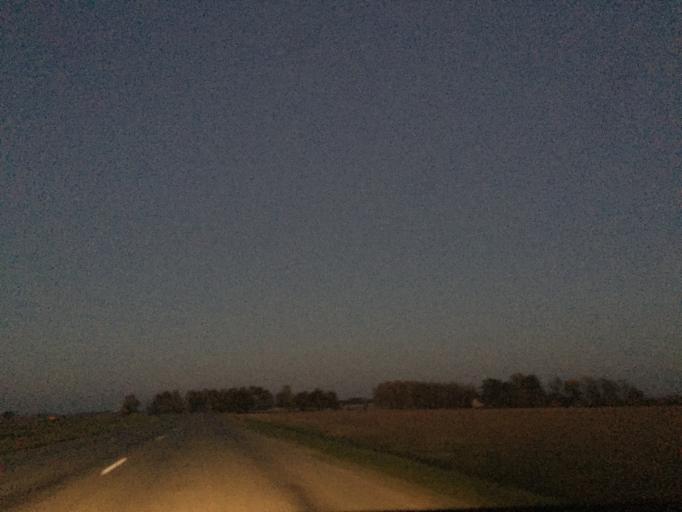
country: LV
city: Tervete
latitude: 56.5298
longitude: 23.3551
